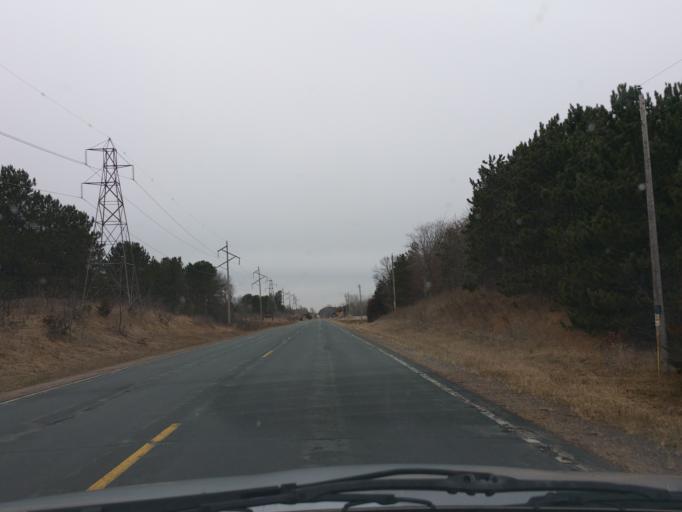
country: US
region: Wisconsin
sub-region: Saint Croix County
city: Roberts
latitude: 45.0357
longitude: -92.6215
